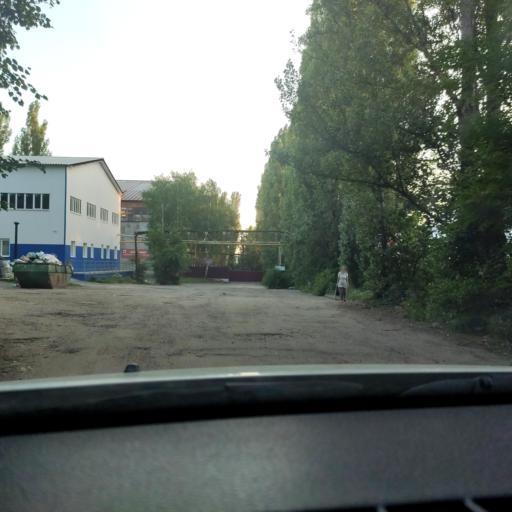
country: RU
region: Voronezj
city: Pridonskoy
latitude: 51.6742
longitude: 39.0851
